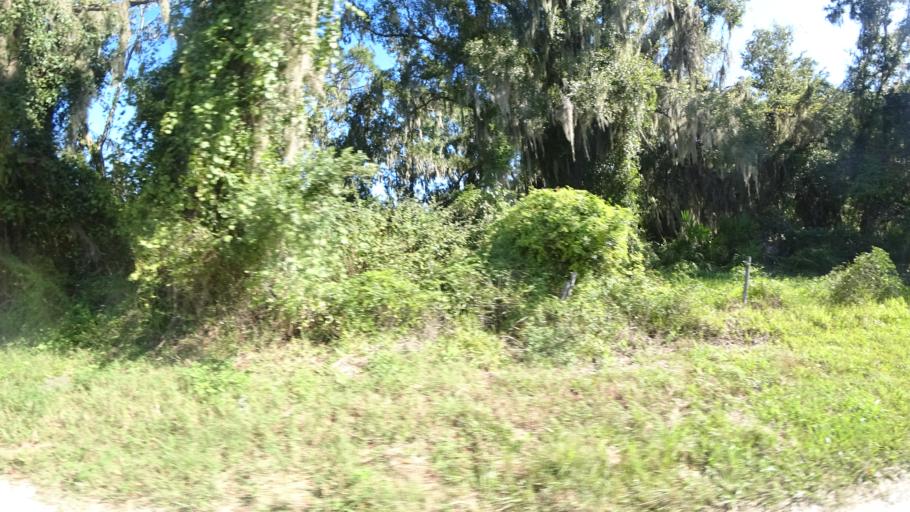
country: US
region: Florida
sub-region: Hillsborough County
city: Wimauma
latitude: 27.5913
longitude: -82.1831
